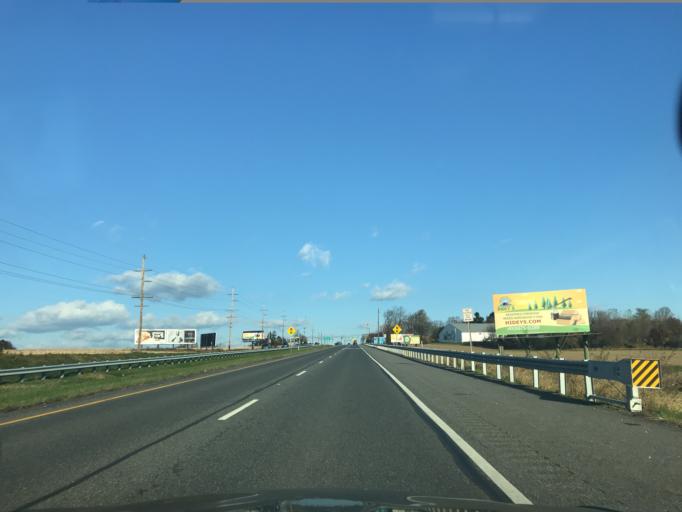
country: US
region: Maryland
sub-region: Carroll County
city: Westminster
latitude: 39.5354
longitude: -76.9287
